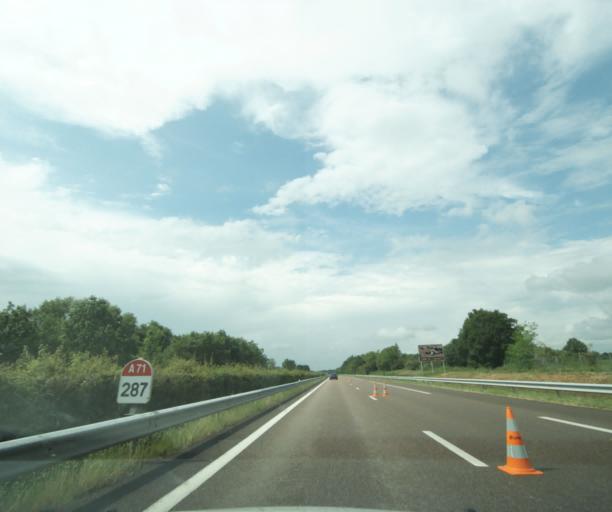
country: FR
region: Auvergne
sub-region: Departement de l'Allier
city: Estivareilles
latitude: 46.4643
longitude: 2.6808
